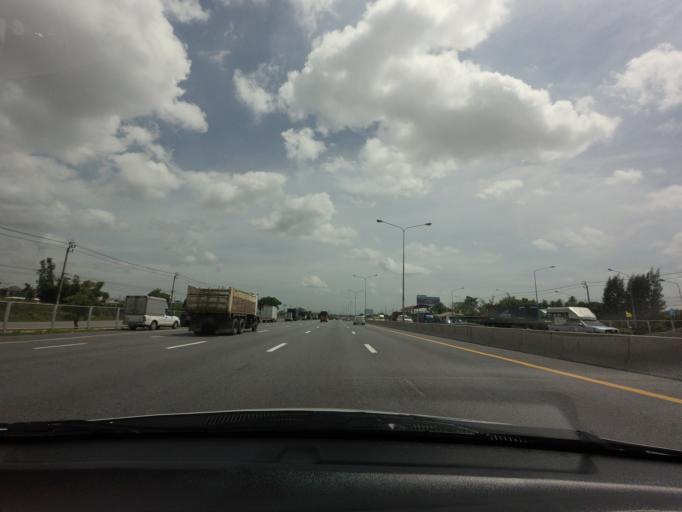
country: TH
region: Bangkok
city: Bang Na
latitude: 13.6908
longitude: 100.6996
